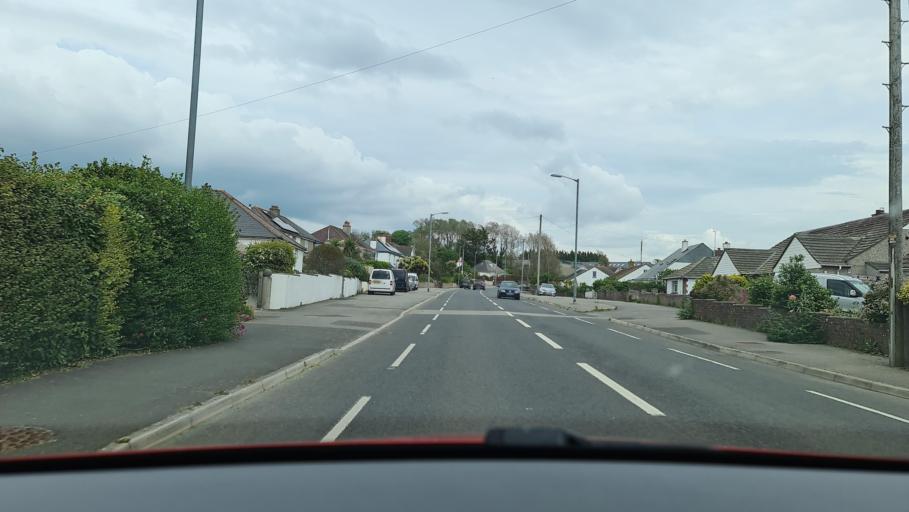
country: GB
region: England
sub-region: Cornwall
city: Bude
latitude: 50.8211
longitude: -4.5368
